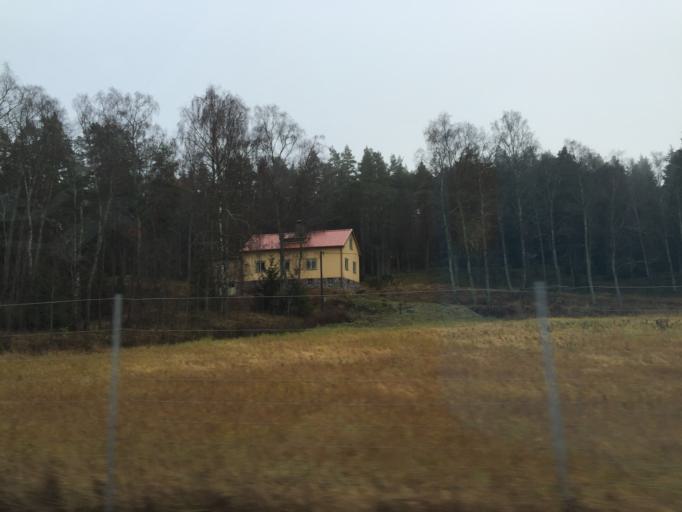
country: SE
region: Stockholm
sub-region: Salems Kommun
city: Ronninge
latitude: 59.1653
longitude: 17.7308
